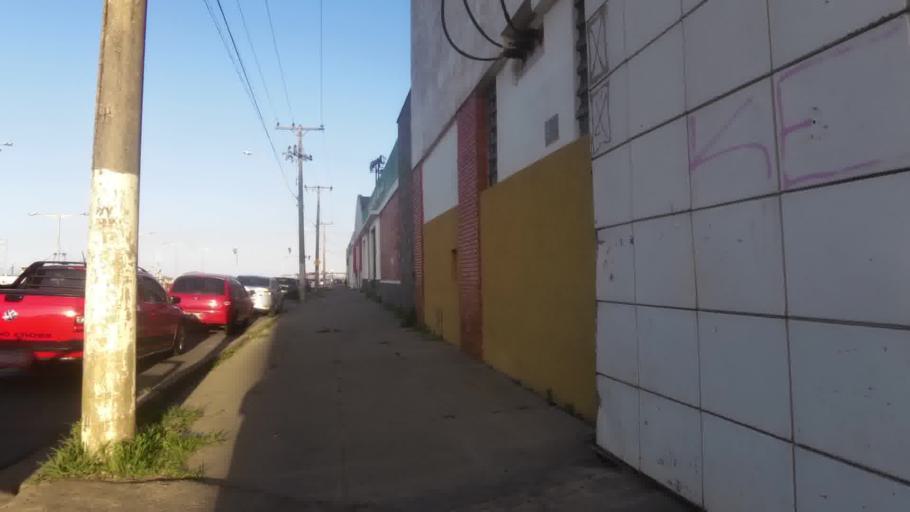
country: BR
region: Rio Grande do Sul
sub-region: Rio Grande
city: Rio Grande
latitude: -32.0286
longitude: -52.1019
